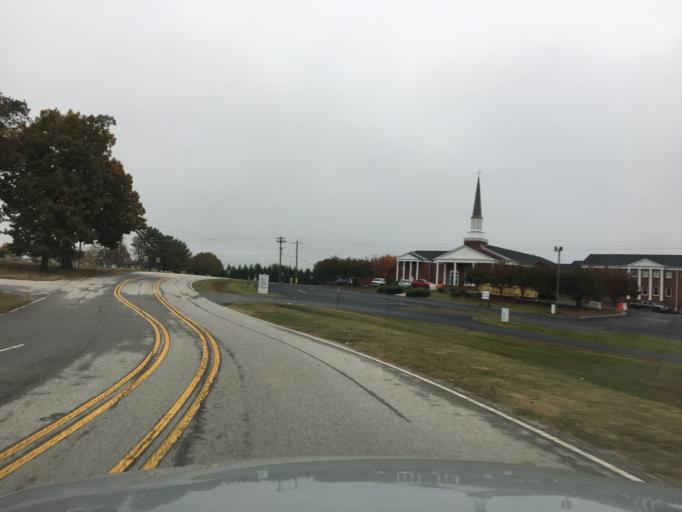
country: US
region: South Carolina
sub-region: Greenville County
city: Five Forks
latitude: 34.8203
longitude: -82.2678
